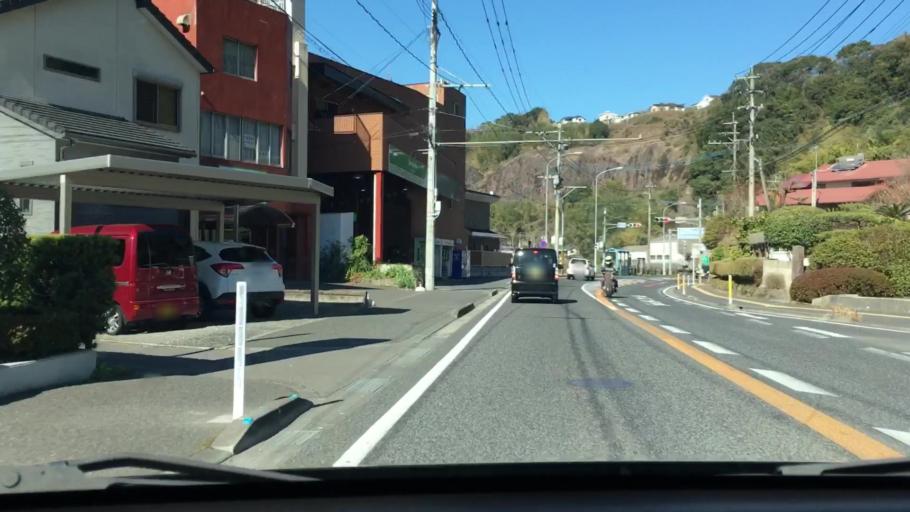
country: JP
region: Kagoshima
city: Kagoshima-shi
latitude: 31.6311
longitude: 130.5242
